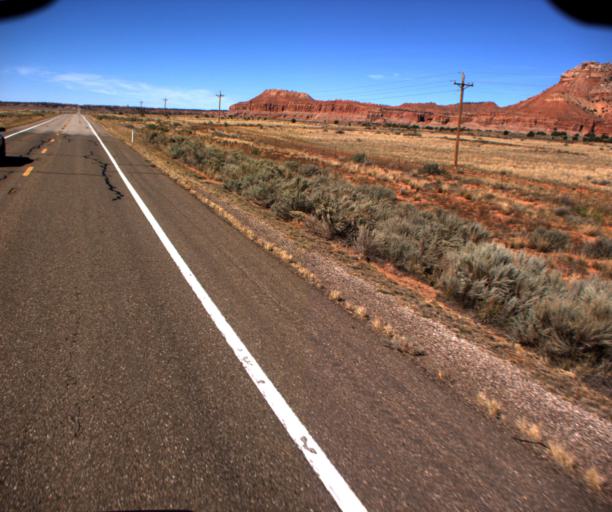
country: US
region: Arizona
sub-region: Mohave County
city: Colorado City
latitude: 36.8655
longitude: -112.8360
